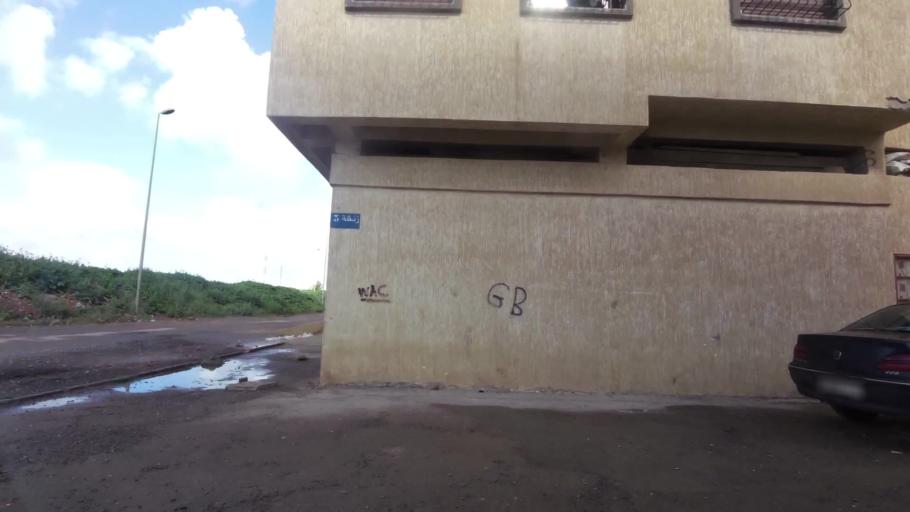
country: MA
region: Grand Casablanca
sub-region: Nouaceur
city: Bouskoura
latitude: 33.5347
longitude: -7.7075
